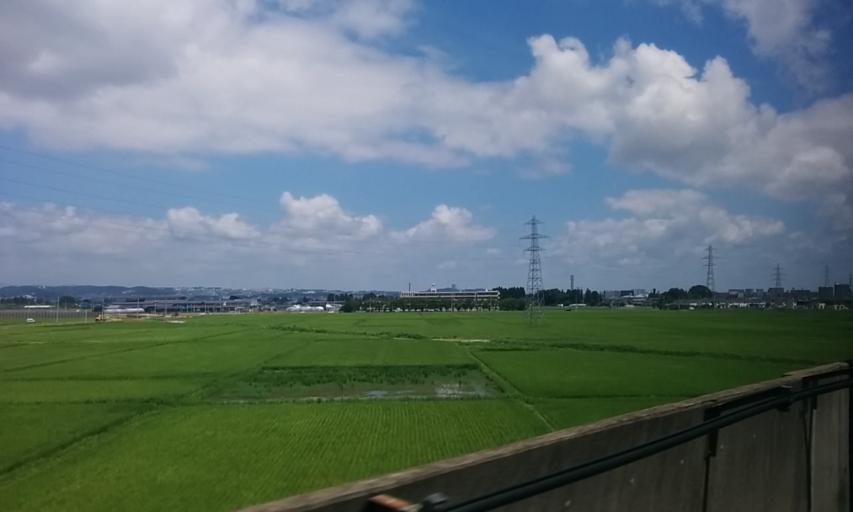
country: JP
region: Miyagi
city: Iwanuma
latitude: 38.1736
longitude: 140.8651
